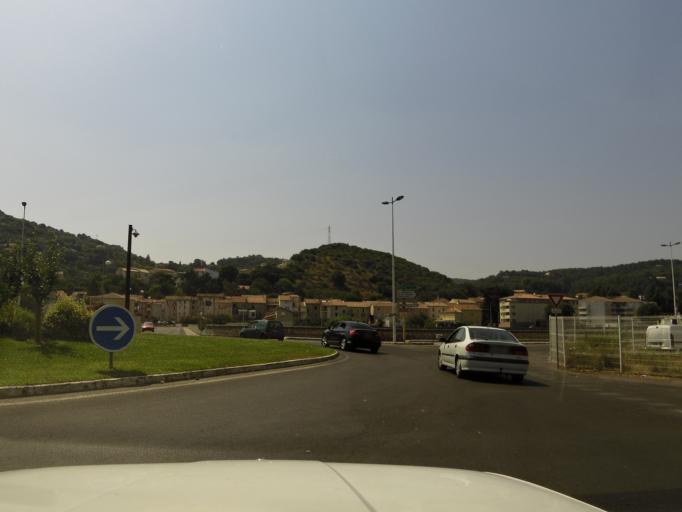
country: FR
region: Languedoc-Roussillon
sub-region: Departement du Gard
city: Ales
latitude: 44.1268
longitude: 4.0737
